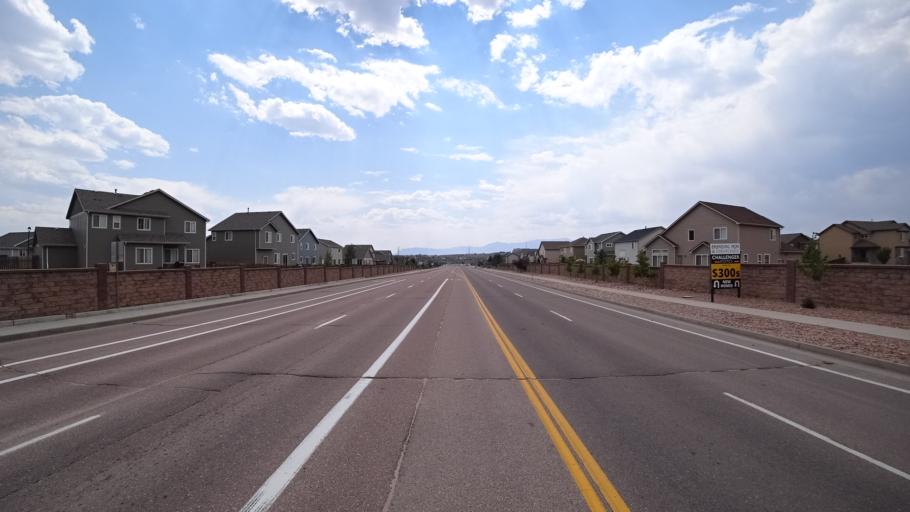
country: US
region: Colorado
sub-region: El Paso County
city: Black Forest
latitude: 38.9490
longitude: -104.6946
